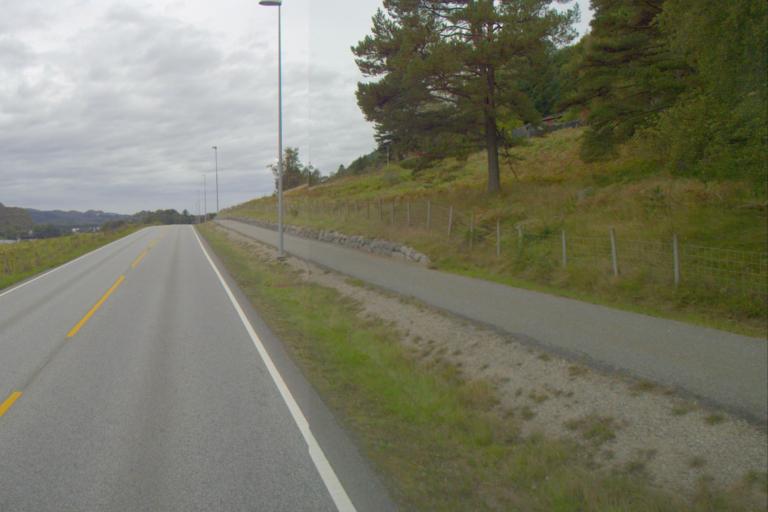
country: NO
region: Rogaland
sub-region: Sandnes
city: Hommersak
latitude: 58.8766
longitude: 5.8250
